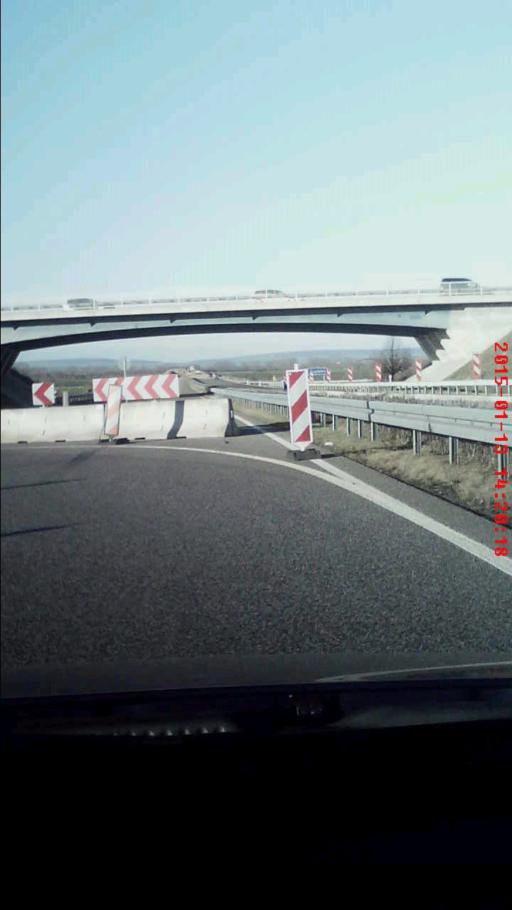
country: DE
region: Thuringia
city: Sprotau
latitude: 51.1540
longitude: 11.1712
